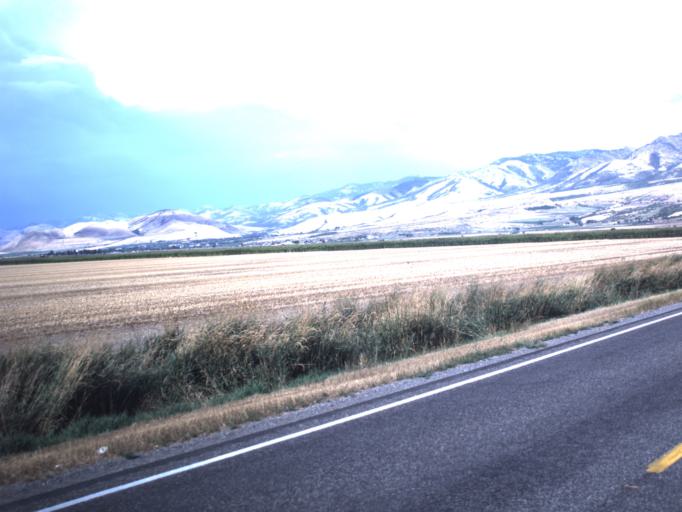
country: US
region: Utah
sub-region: Cache County
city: Lewiston
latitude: 41.9760
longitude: -111.8411
